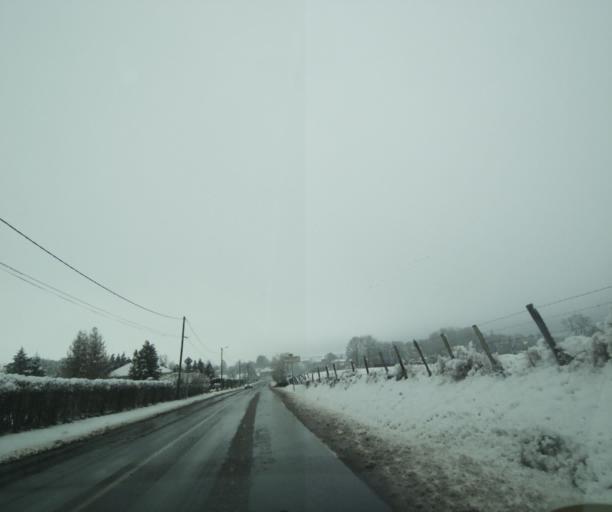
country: FR
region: Champagne-Ardenne
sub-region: Departement de la Haute-Marne
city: Montier-en-Der
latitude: 48.5373
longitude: 4.8206
